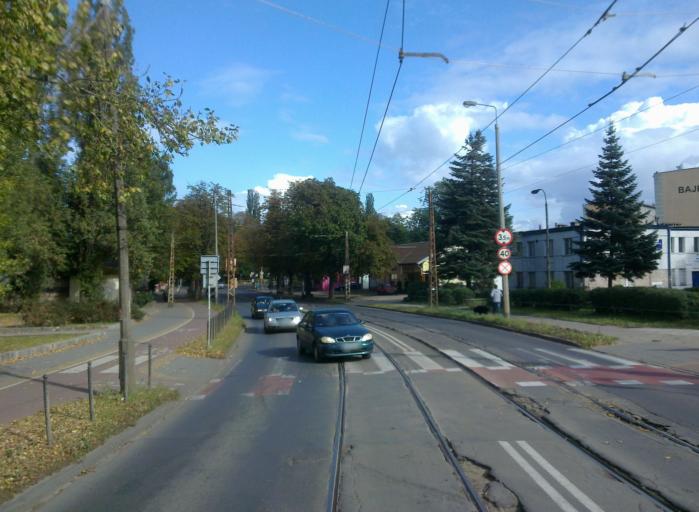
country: PL
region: Pomeranian Voivodeship
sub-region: Gdansk
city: Gdansk
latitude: 54.3568
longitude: 18.6813
